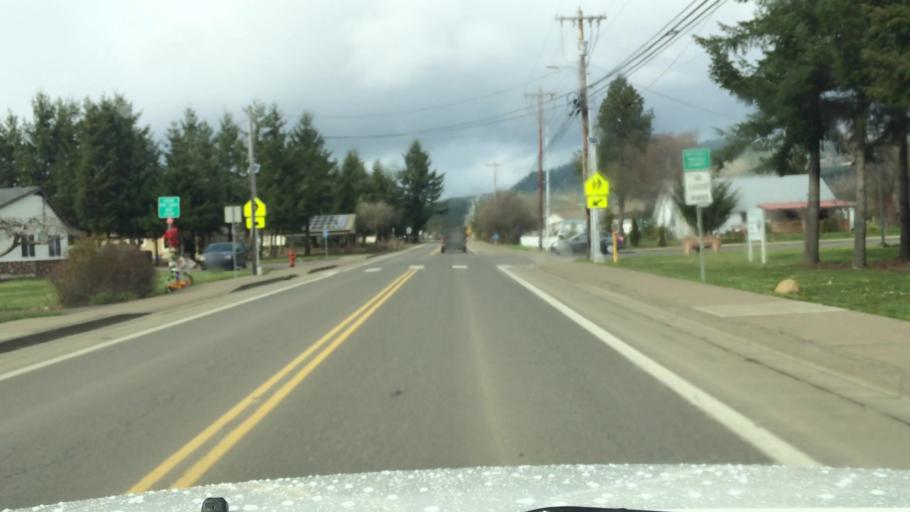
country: US
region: Oregon
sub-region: Polk County
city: Grand Ronde
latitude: 45.0758
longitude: -123.6119
